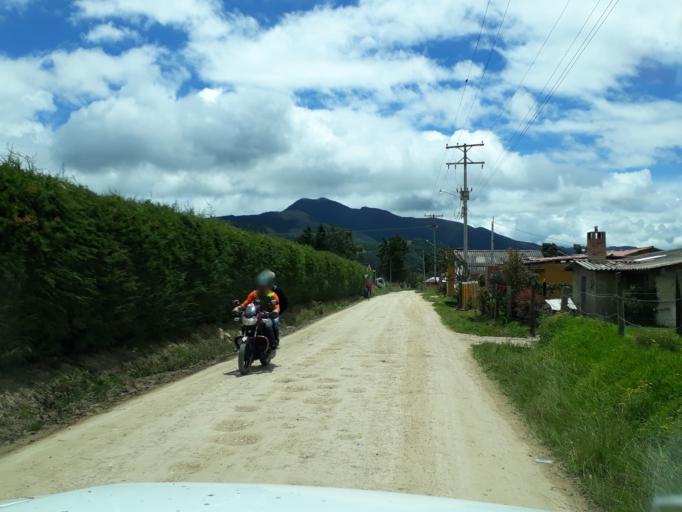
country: CO
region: Cundinamarca
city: Guasca
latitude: 4.8440
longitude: -73.9023
